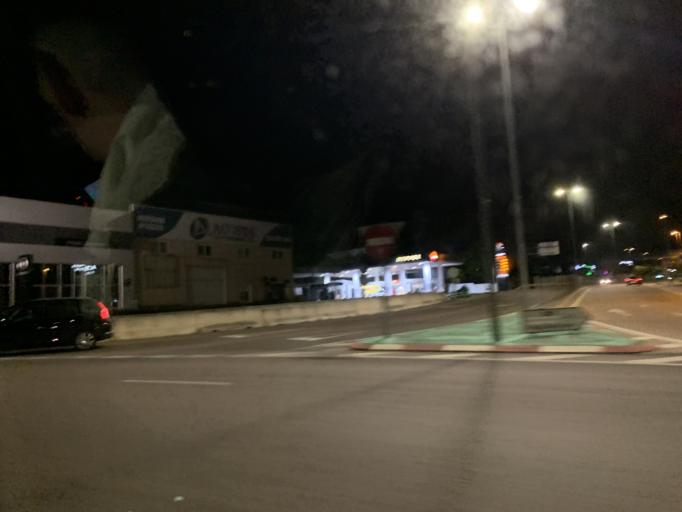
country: ES
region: Extremadura
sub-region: Provincia de Badajoz
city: Badajoz
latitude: 38.8786
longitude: -6.9454
